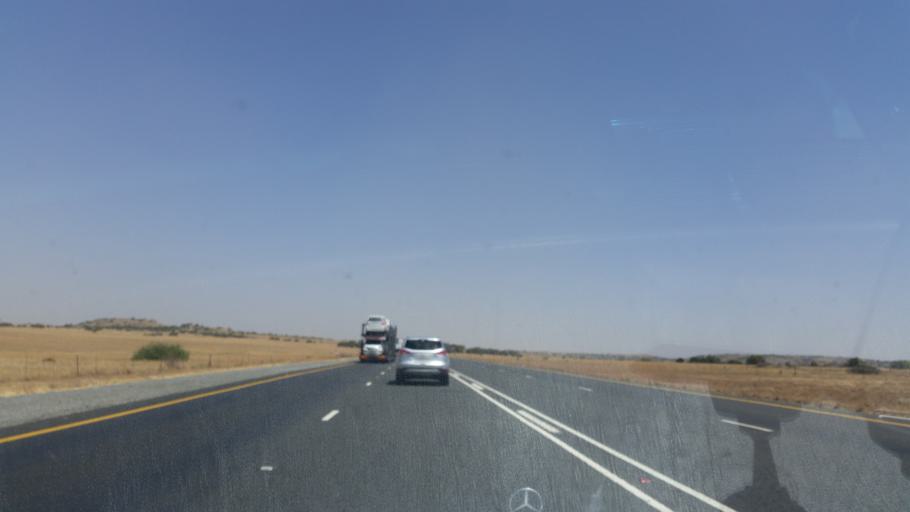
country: ZA
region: Orange Free State
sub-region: Lejweleputswa District Municipality
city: Winburg
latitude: -28.6914
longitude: 26.8131
